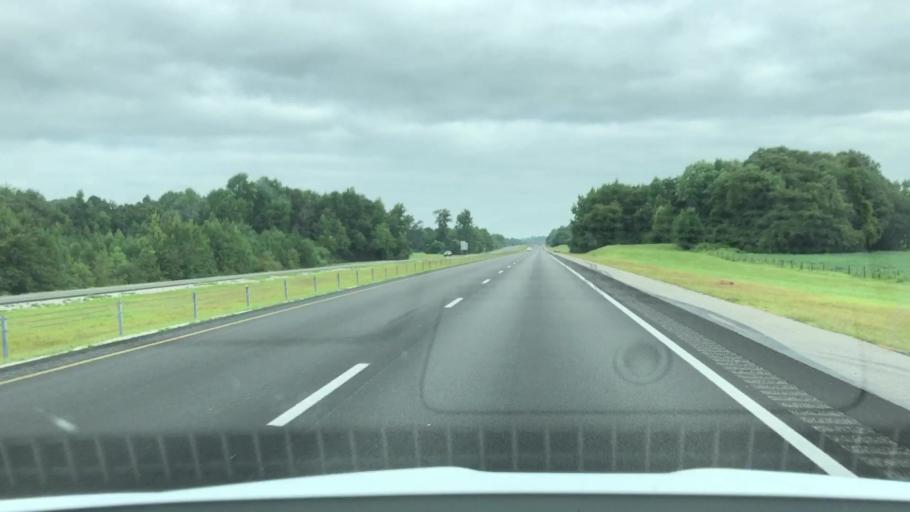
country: US
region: North Carolina
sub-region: Wayne County
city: Fremont
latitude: 35.5640
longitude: -77.9879
